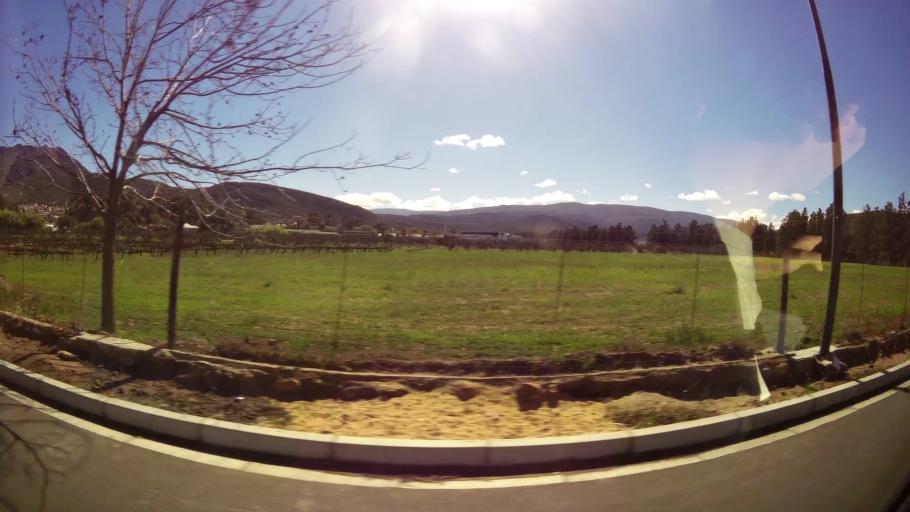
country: ZA
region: Western Cape
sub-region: Cape Winelands District Municipality
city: Ashton
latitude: -33.7875
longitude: 20.1305
